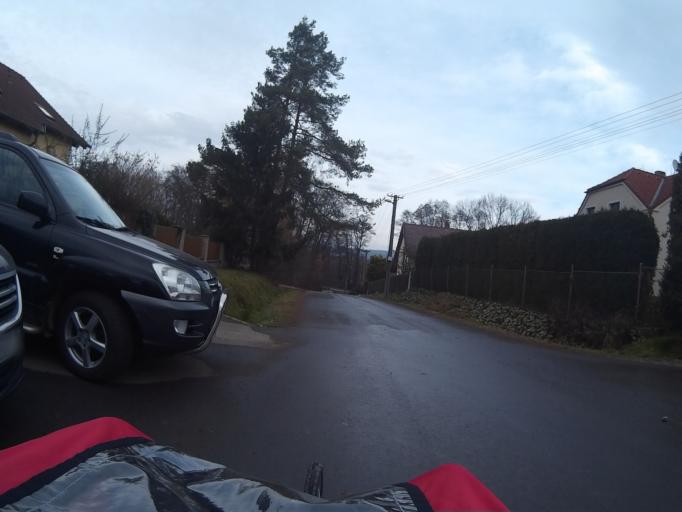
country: CZ
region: Plzensky
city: St'ahlavy
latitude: 49.6725
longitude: 13.4966
